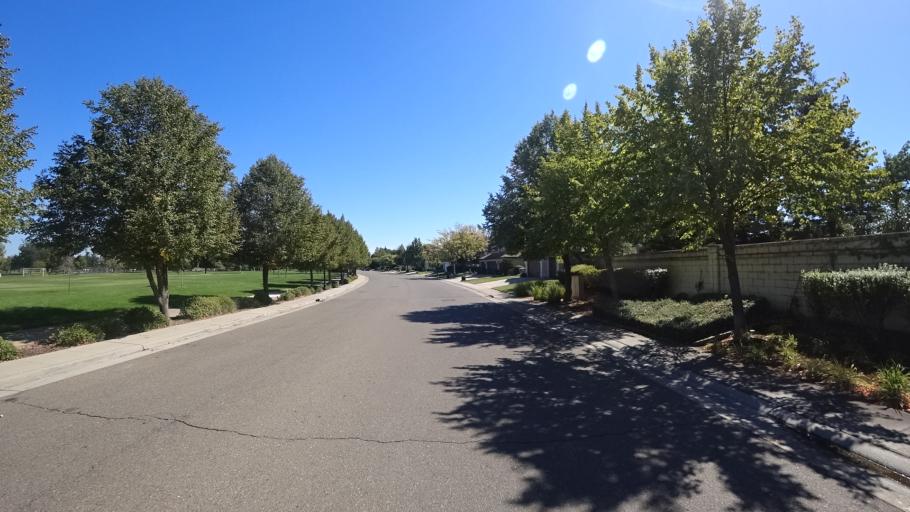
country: US
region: California
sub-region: Sacramento County
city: Laguna
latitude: 38.4106
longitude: -121.4674
